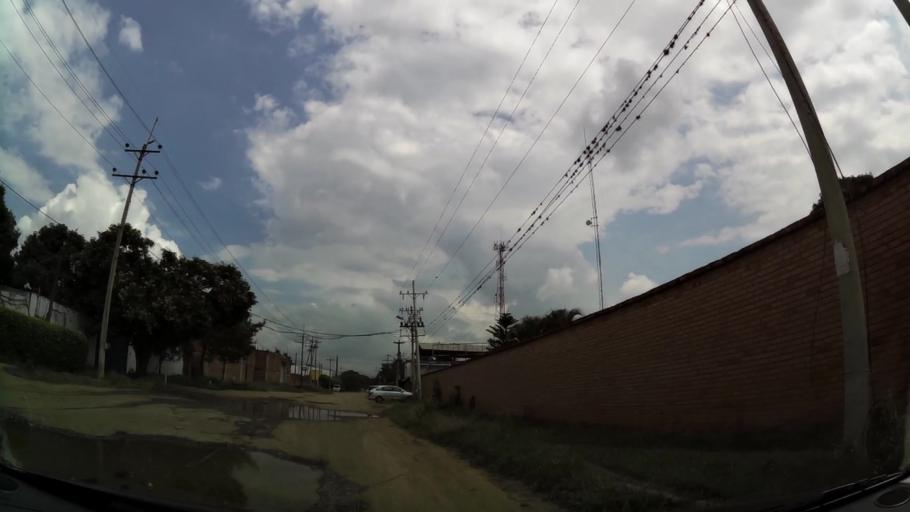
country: CO
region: Valle del Cauca
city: Cali
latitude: 3.4954
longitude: -76.4730
